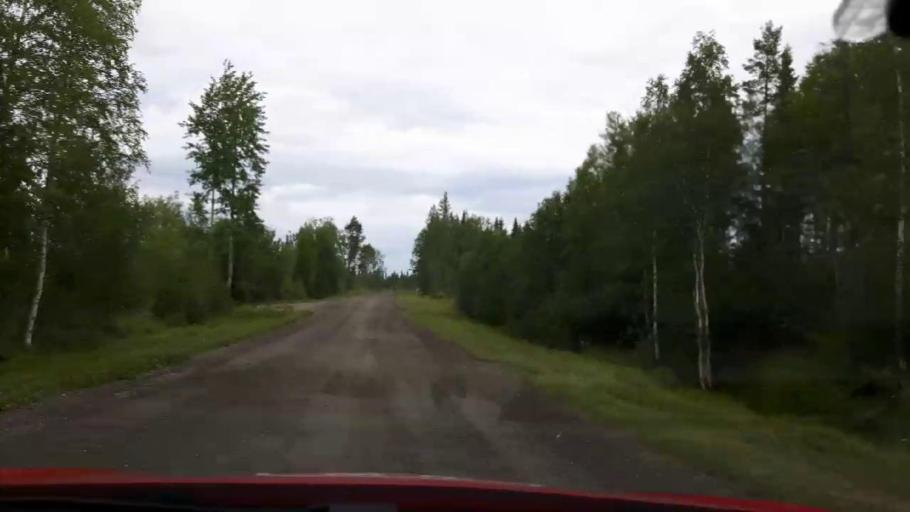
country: SE
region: Jaemtland
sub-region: Stroemsunds Kommun
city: Stroemsund
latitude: 63.8009
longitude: 15.6141
